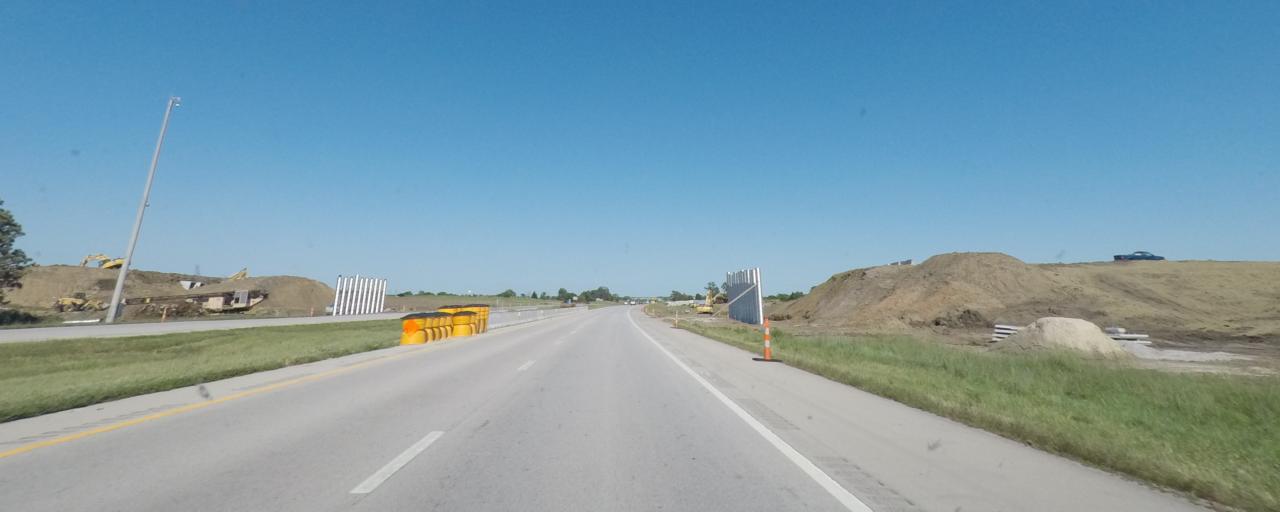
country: US
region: Kansas
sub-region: Johnson County
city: Edgerton
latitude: 38.7459
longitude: -95.0022
